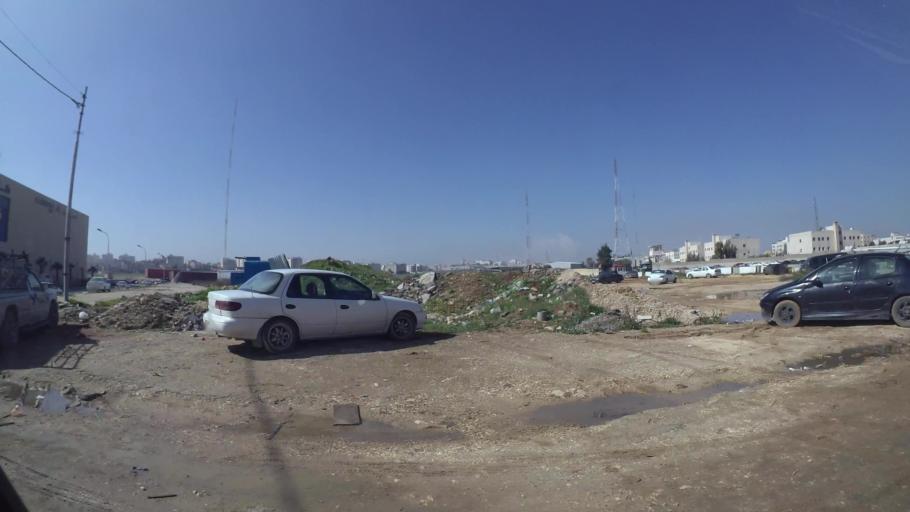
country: JO
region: Amman
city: Al Bunayyat ash Shamaliyah
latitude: 31.9050
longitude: 35.8871
